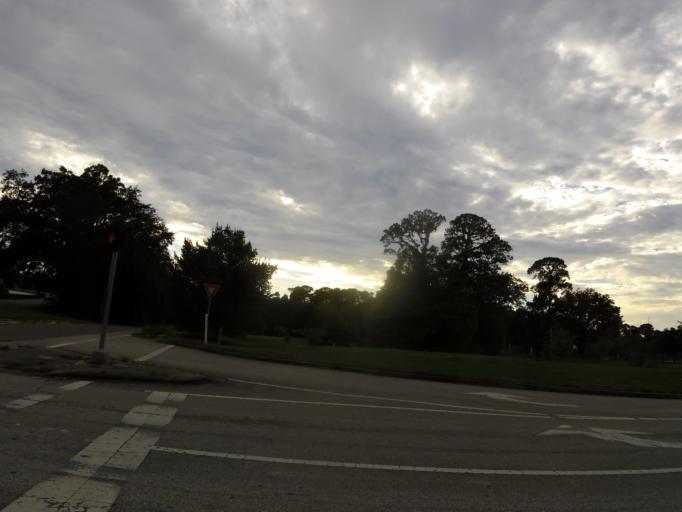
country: US
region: Florida
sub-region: Duval County
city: Jacksonville
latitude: 30.2968
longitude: -81.7181
